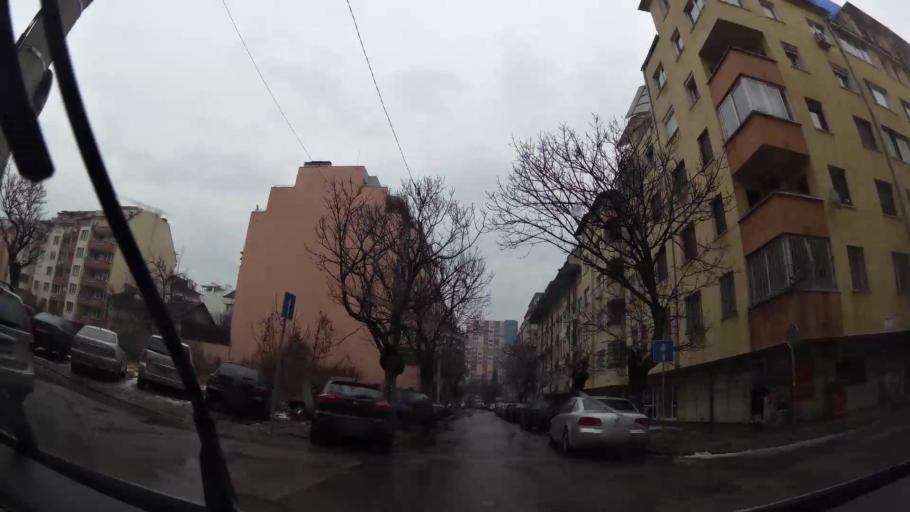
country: BG
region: Sofia-Capital
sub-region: Stolichna Obshtina
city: Sofia
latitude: 42.6768
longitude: 23.2921
